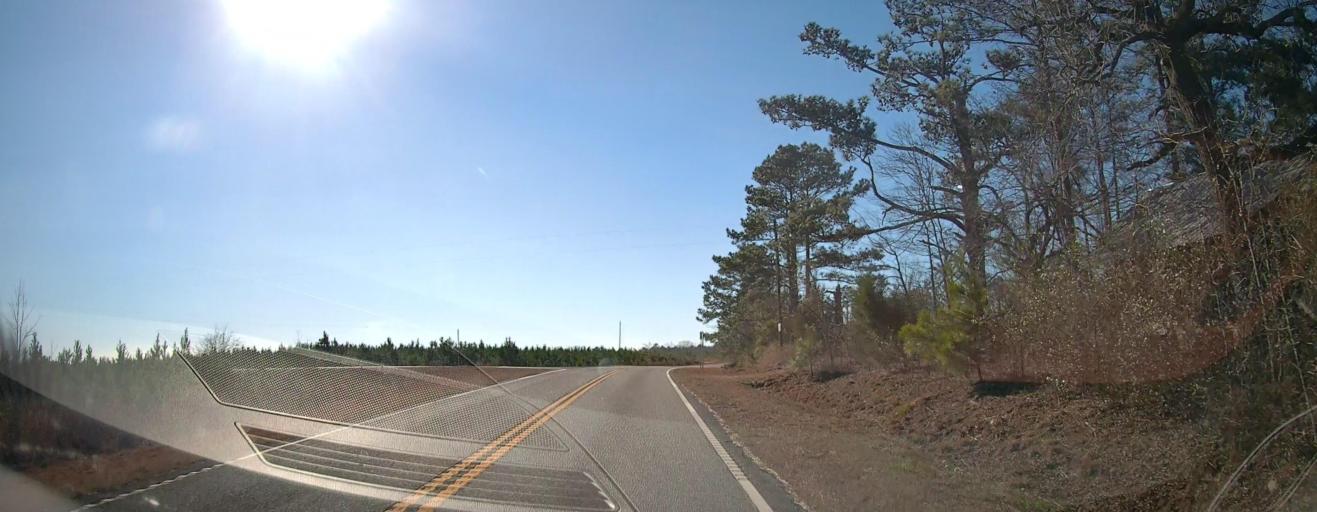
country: US
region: Georgia
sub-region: Talbot County
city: Talbotton
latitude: 32.6459
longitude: -84.4175
